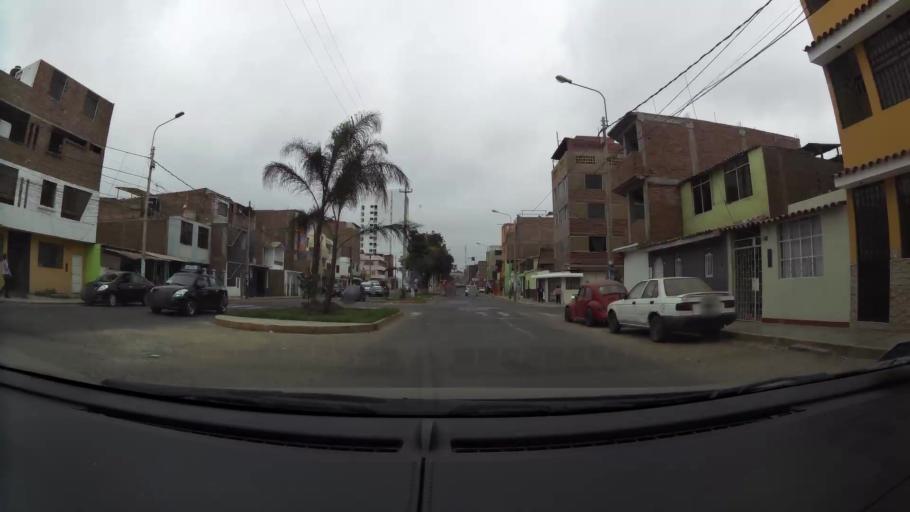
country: PE
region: La Libertad
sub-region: Provincia de Trujillo
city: Trujillo
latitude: -8.1193
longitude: -79.0281
